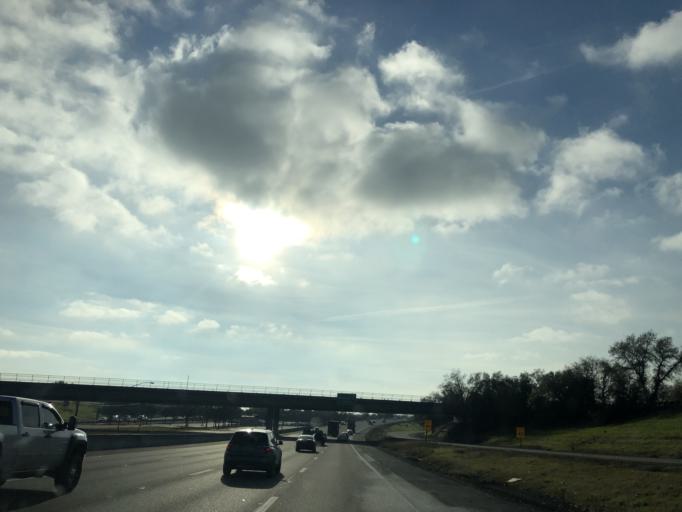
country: US
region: California
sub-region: Sacramento County
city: Arden-Arcade
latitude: 38.6415
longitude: -121.3980
